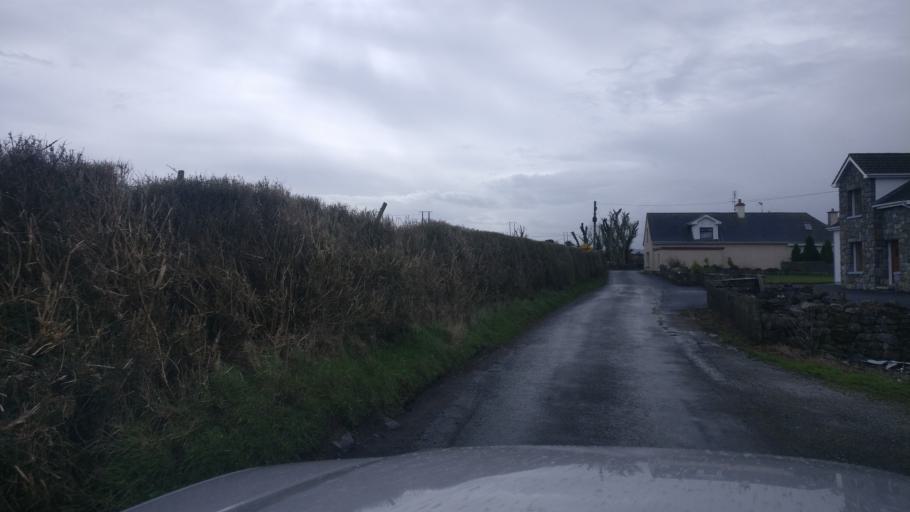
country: IE
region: Connaught
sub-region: County Galway
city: Loughrea
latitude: 53.2004
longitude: -8.6064
